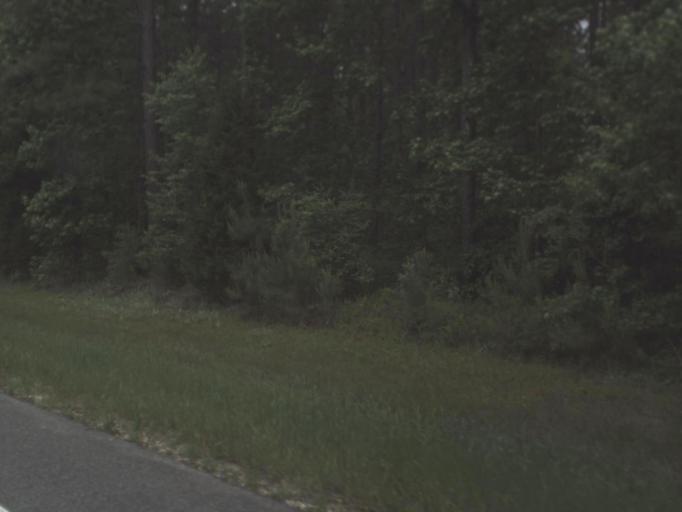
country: US
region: Florida
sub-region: Calhoun County
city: Blountstown
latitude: 30.3357
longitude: -85.1225
